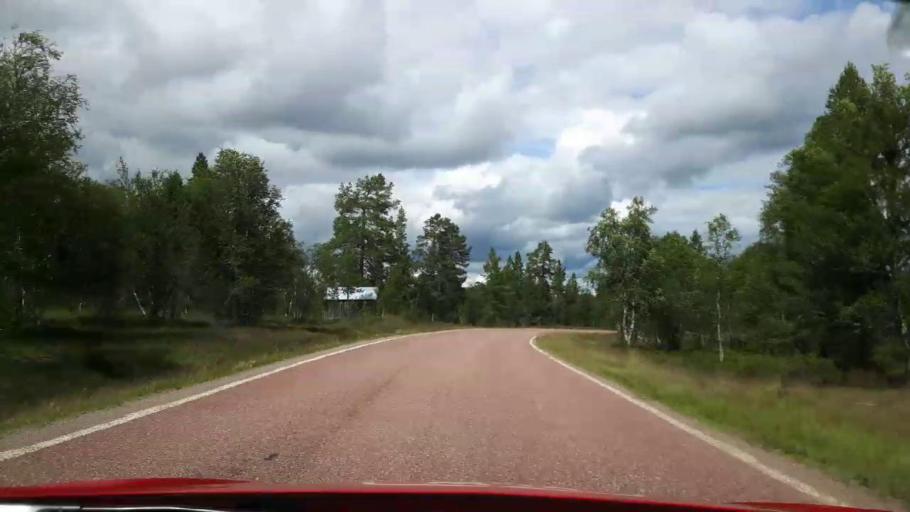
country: NO
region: Hedmark
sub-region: Trysil
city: Innbygda
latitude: 62.0955
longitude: 12.9725
